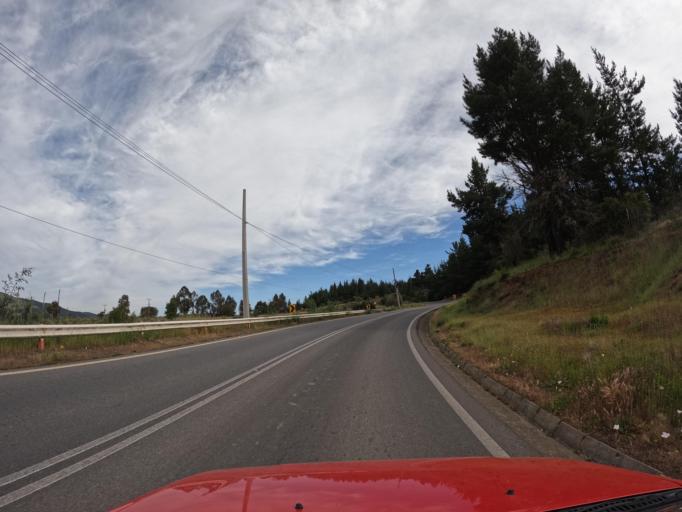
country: CL
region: Maule
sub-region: Provincia de Talca
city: Talca
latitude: -35.3256
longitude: -71.9299
